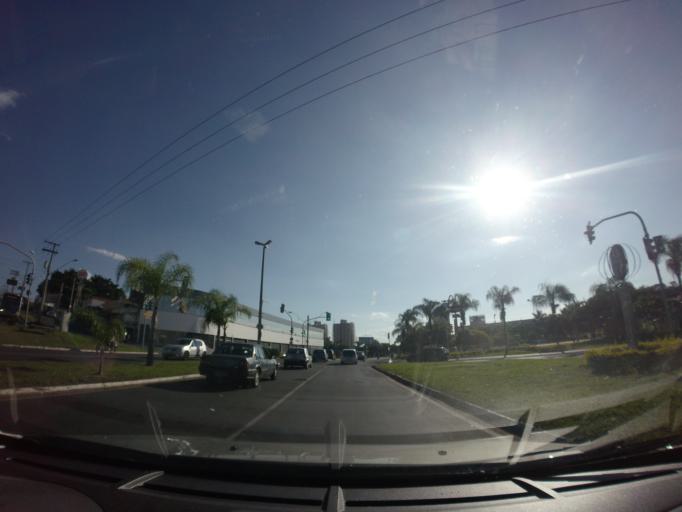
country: BR
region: Sao Paulo
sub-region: Rio Claro
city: Rio Claro
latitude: -22.4134
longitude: -47.5699
